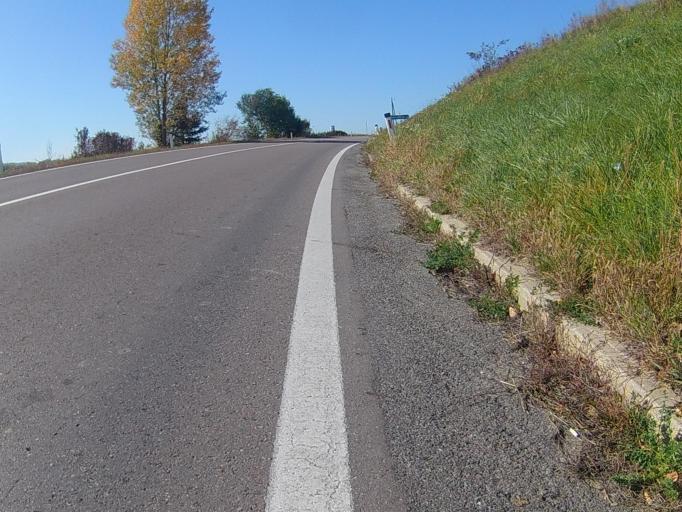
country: SI
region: Sveti Jurij v Slovenskih Goricah
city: Jurovski Dol
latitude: 46.5660
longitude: 15.7724
